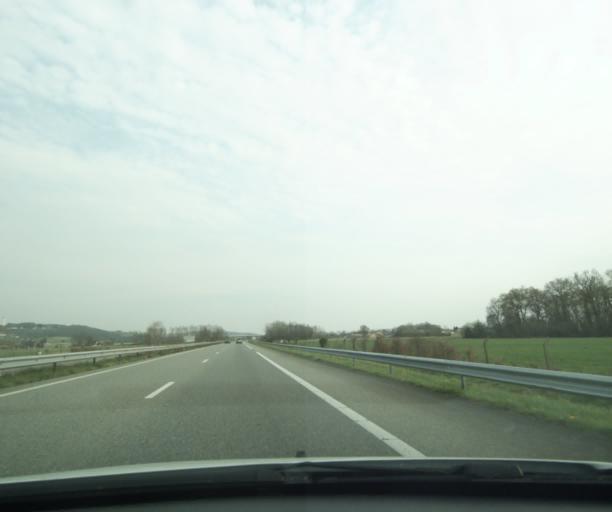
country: FR
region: Aquitaine
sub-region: Departement des Pyrenees-Atlantiques
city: Artix
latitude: 43.4135
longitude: -0.5721
